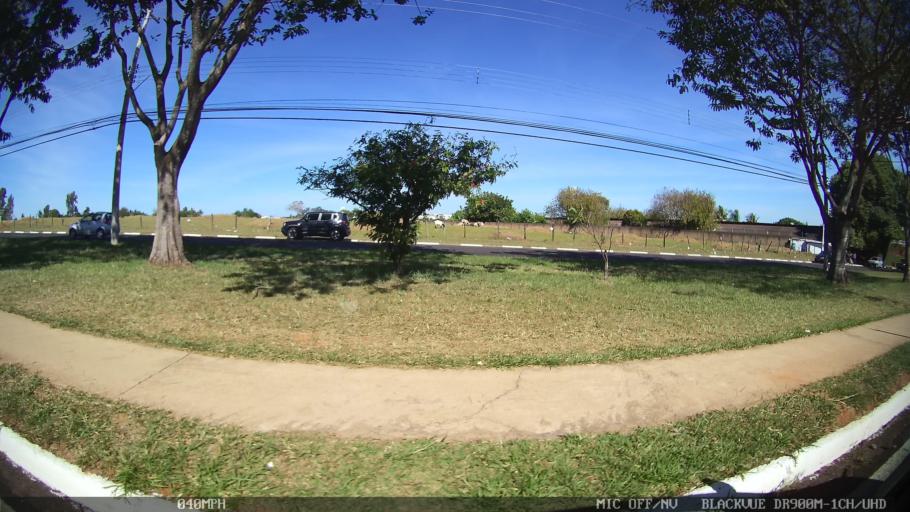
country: BR
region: Sao Paulo
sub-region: Franca
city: Franca
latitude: -20.5568
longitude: -47.3833
